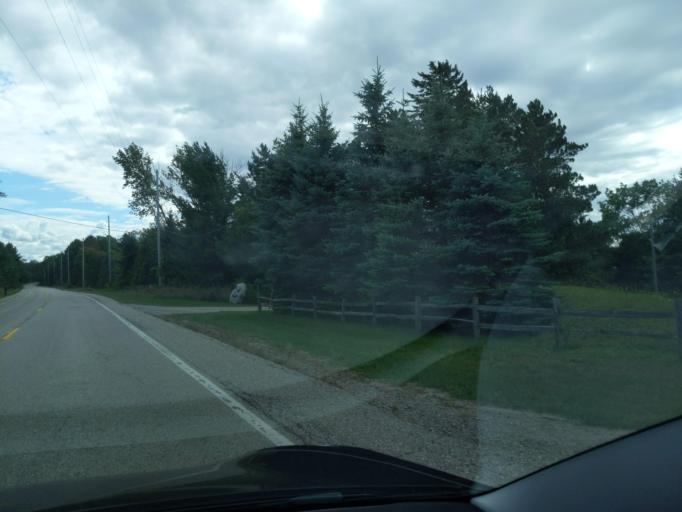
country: US
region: Michigan
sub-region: Kalkaska County
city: Rapid City
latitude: 44.9090
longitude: -85.2825
